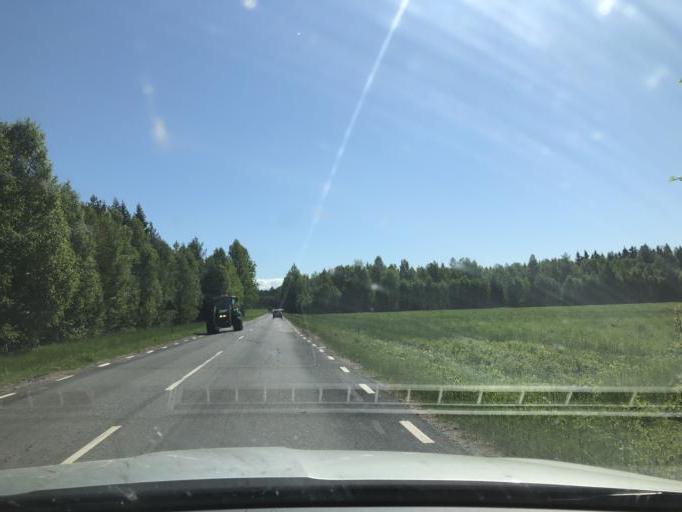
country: SE
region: Norrbotten
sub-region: Lulea Kommun
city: Gammelstad
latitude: 65.6607
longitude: 21.9826
